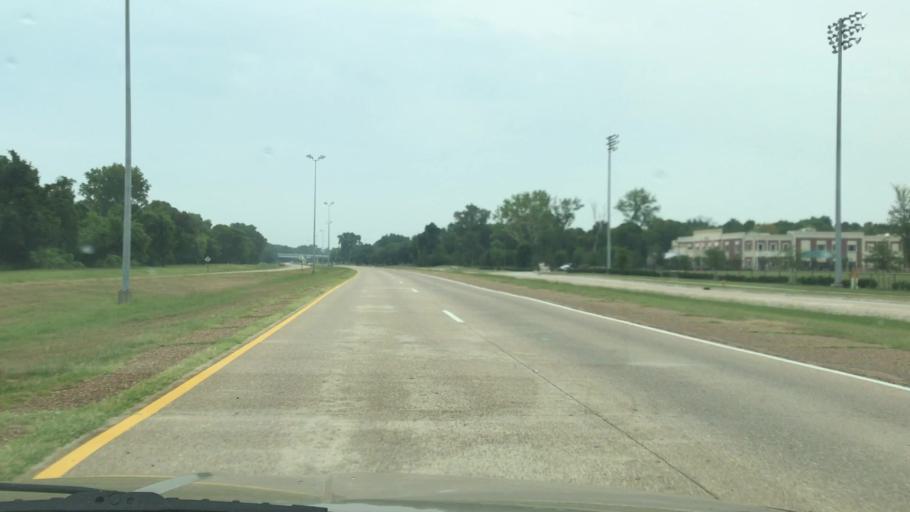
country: US
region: Louisiana
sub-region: Bossier Parish
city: Bossier City
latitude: 32.4973
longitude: -93.7119
